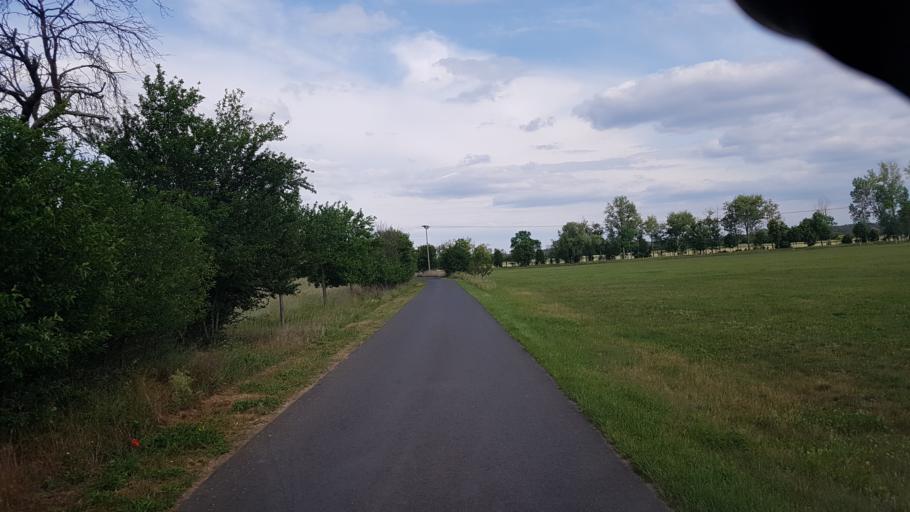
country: DE
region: Brandenburg
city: Herzberg
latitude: 51.7193
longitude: 13.2811
